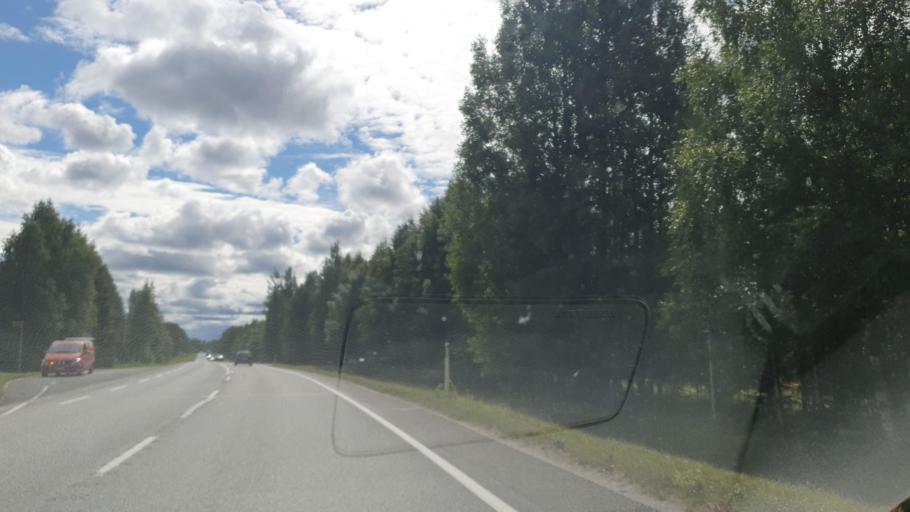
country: FI
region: Kainuu
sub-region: Kajaani
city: Kajaani
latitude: 64.1462
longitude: 27.5029
